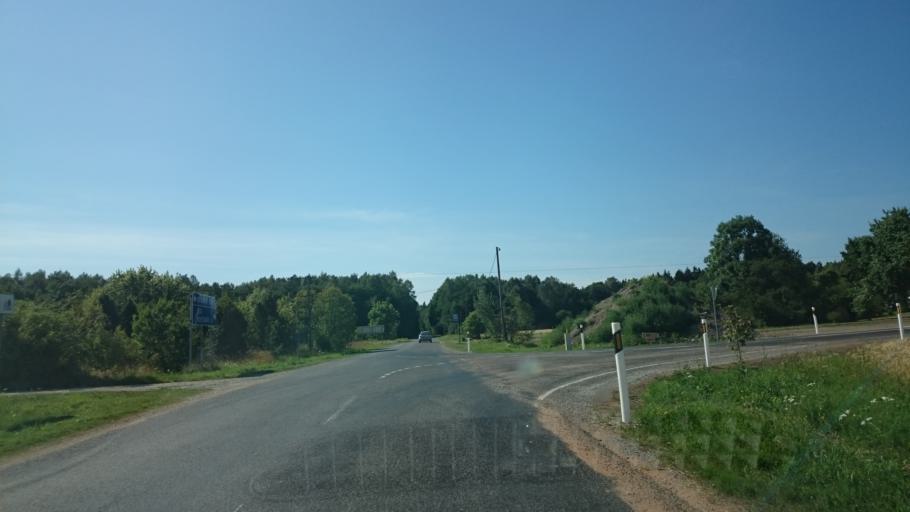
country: EE
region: Saare
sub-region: Orissaare vald
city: Orissaare
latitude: 58.5787
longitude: 22.7064
